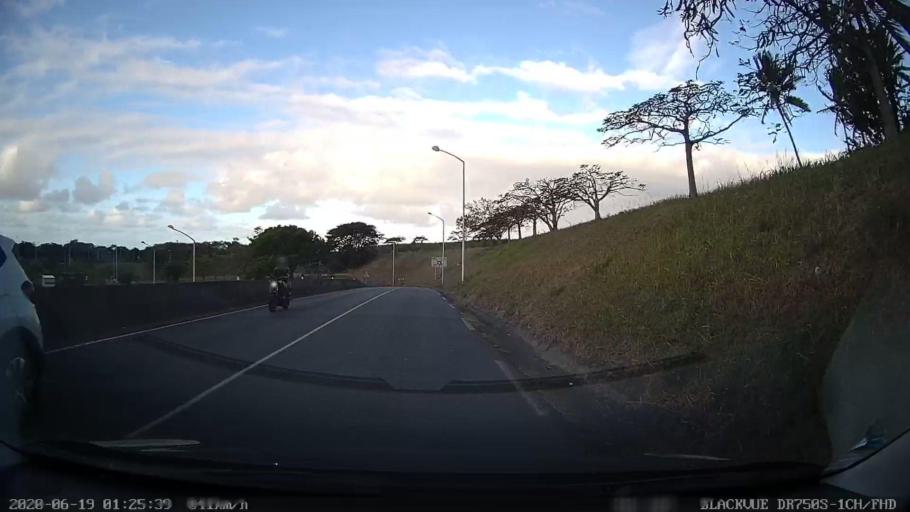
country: RE
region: Reunion
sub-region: Reunion
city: Sainte-Marie
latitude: -20.8992
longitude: 55.5102
